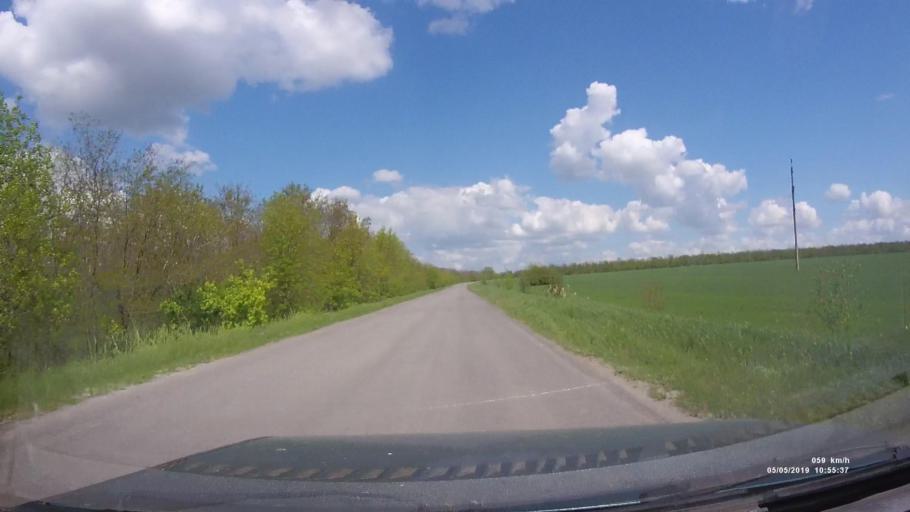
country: RU
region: Rostov
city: Ust'-Donetskiy
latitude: 47.6671
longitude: 40.8207
